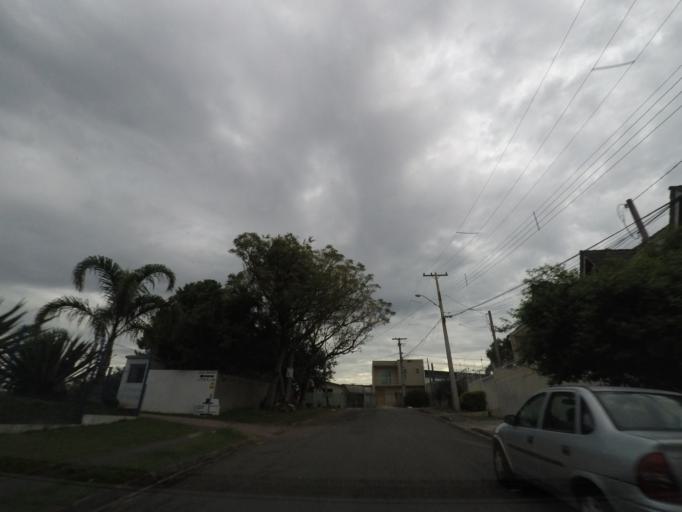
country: BR
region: Parana
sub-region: Curitiba
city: Curitiba
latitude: -25.4691
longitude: -49.3121
